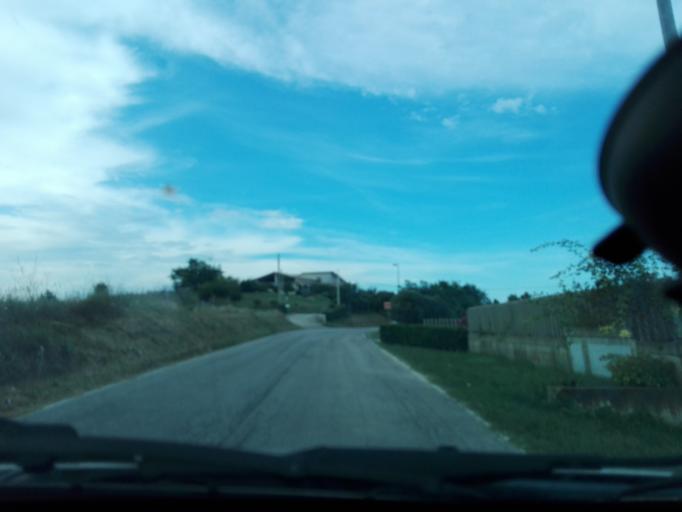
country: IT
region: Abruzzo
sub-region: Provincia di Pescara
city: Cappelle sul Tavo
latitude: 42.4561
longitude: 14.1126
